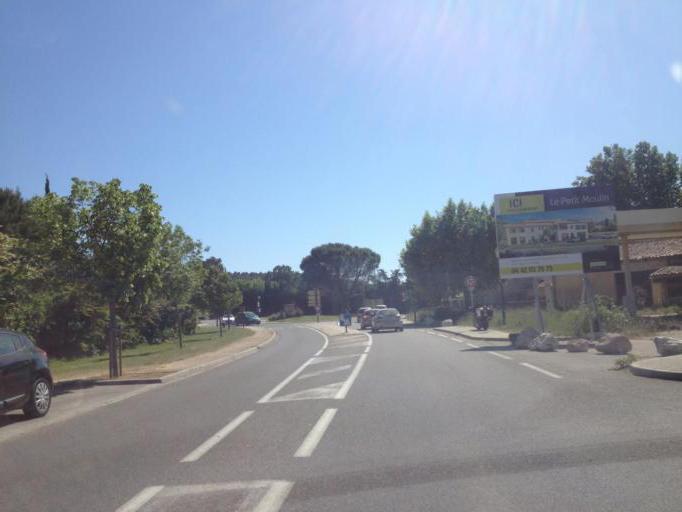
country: FR
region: Provence-Alpes-Cote d'Azur
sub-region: Departement du Vaucluse
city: Lourmarin
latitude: 43.7627
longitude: 5.3652
